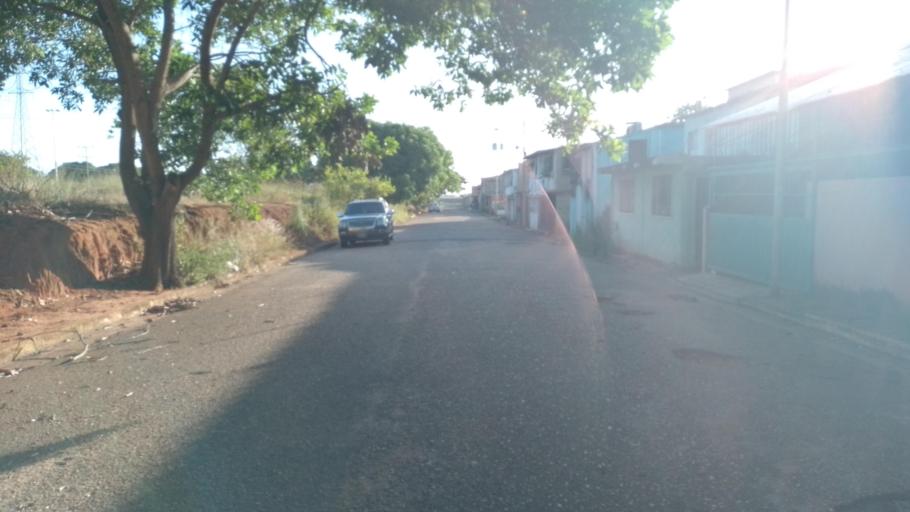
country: VE
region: Anzoategui
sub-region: Municipio San Jose de Guanipa
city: San Jose de Guanipa
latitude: 8.8886
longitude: -64.1976
